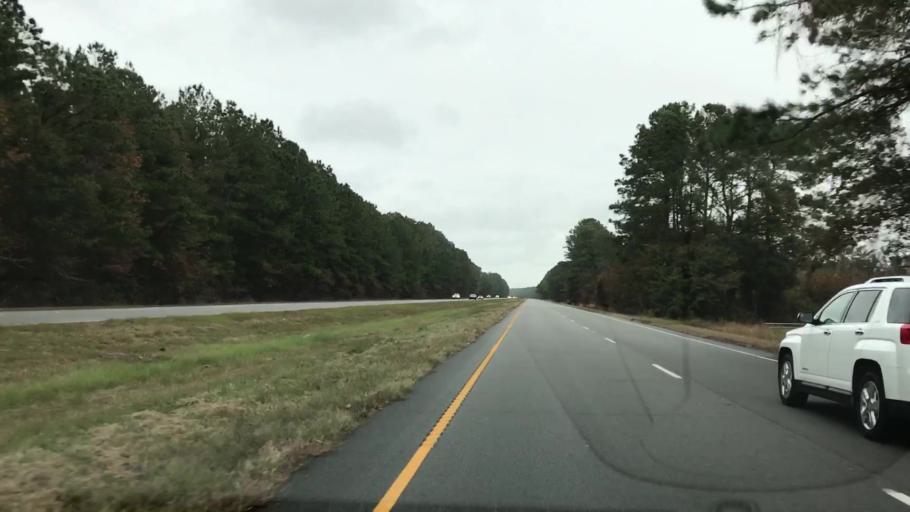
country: US
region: South Carolina
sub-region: Charleston County
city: Awendaw
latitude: 33.1122
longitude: -79.4592
